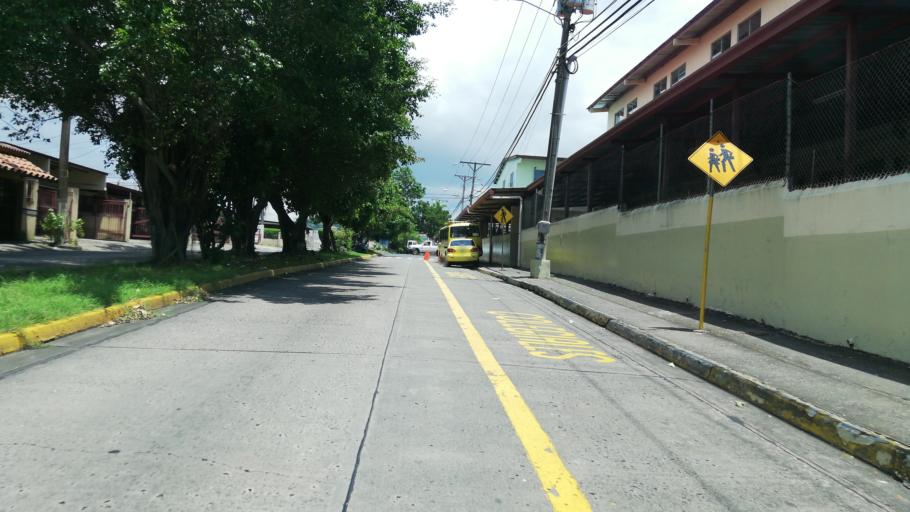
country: PA
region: Panama
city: San Miguelito
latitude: 9.0551
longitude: -79.4552
